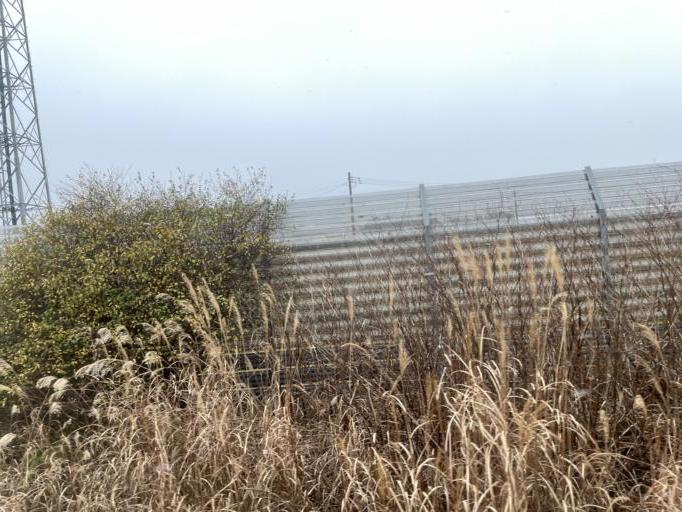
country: JP
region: Aomori
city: Aomori Shi
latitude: 40.9701
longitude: 140.6545
